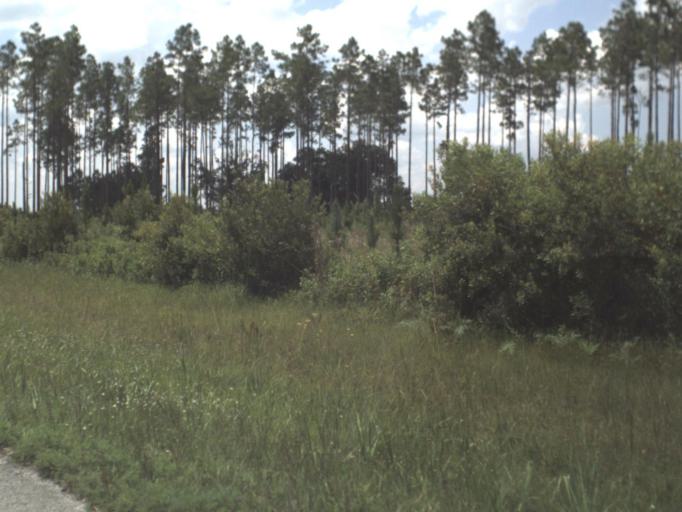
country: US
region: Florida
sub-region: Baker County
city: Macclenny
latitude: 30.5407
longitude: -82.3359
